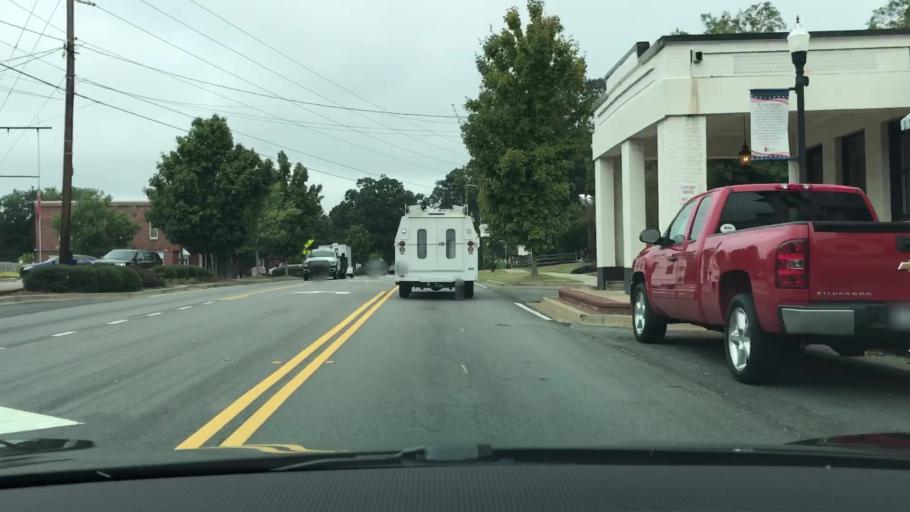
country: US
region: Georgia
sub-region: Oconee County
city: Watkinsville
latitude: 33.8633
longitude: -83.4093
